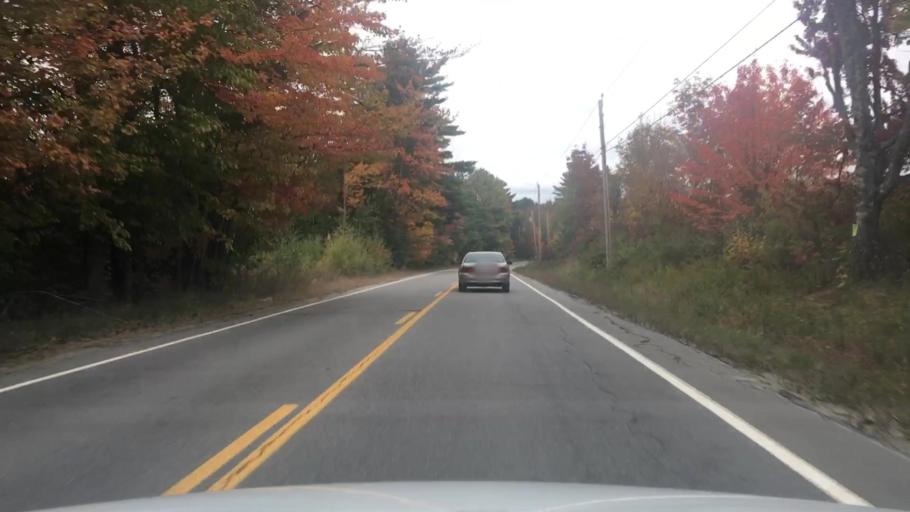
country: US
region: Maine
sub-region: Kennebec County
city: Oakland
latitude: 44.5423
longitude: -69.7939
